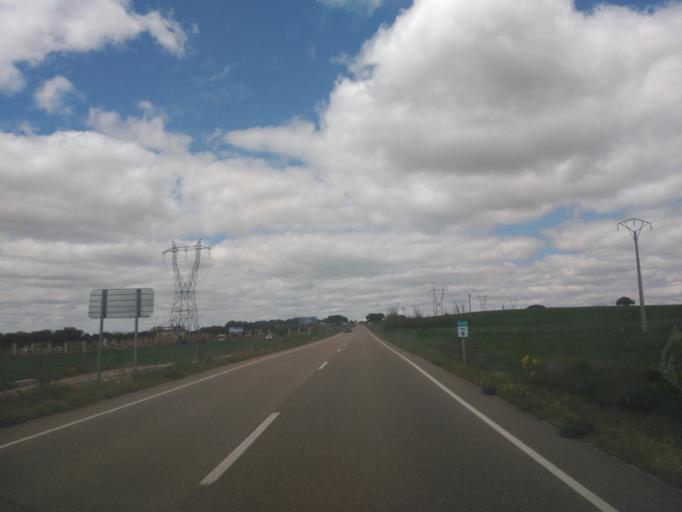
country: ES
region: Castille and Leon
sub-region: Provincia de Salamanca
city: Florida de Liebana
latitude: 41.0290
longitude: -5.7281
